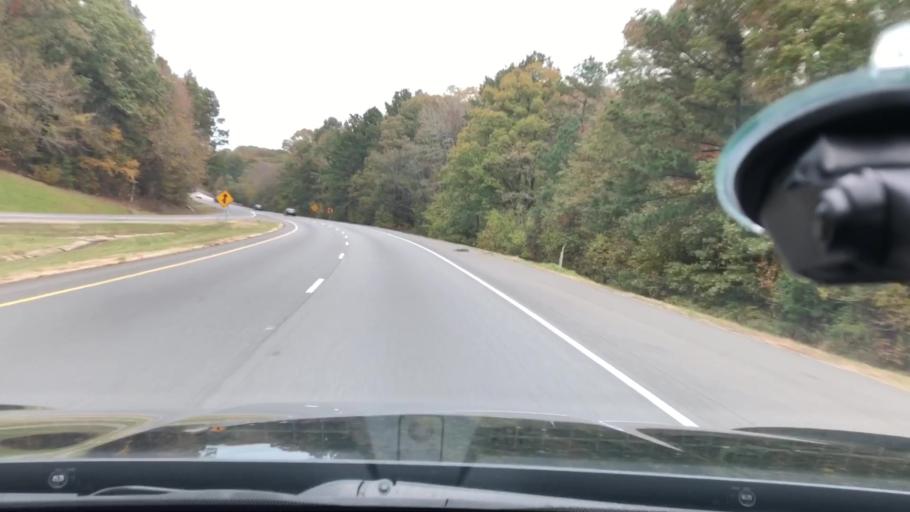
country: US
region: Arkansas
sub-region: Hot Spring County
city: Malvern
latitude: 34.3512
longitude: -92.8879
